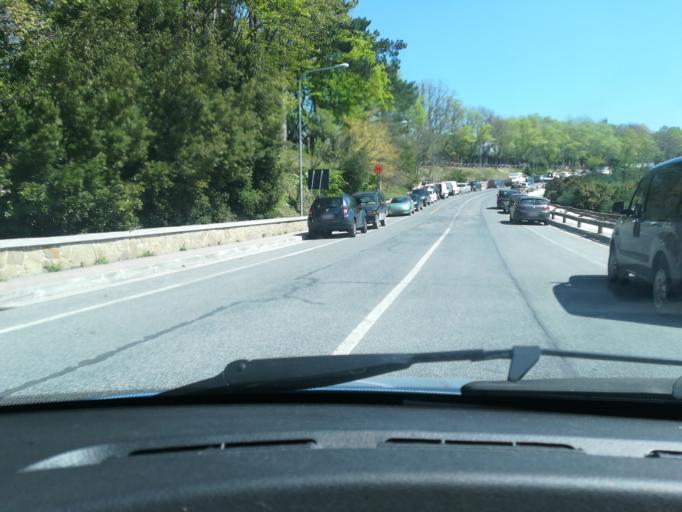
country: IT
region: The Marches
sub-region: Provincia di Macerata
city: Cingoli
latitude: 43.3754
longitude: 13.2099
